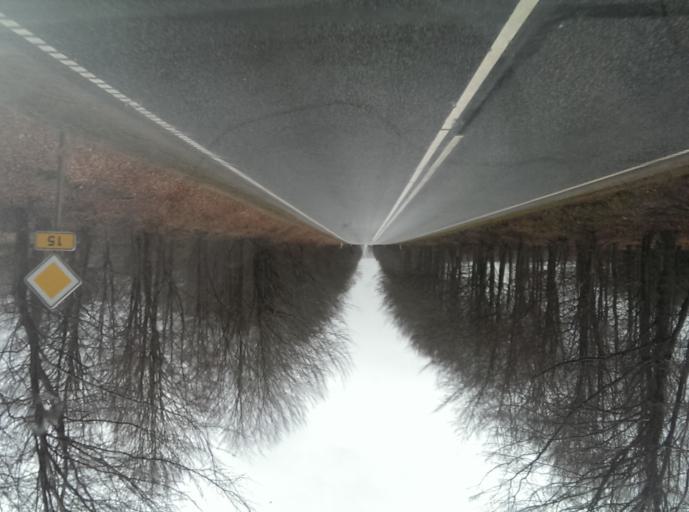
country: DK
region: Central Jutland
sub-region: Ringkobing-Skjern Kommune
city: Skjern
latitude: 56.0833
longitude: 8.4266
